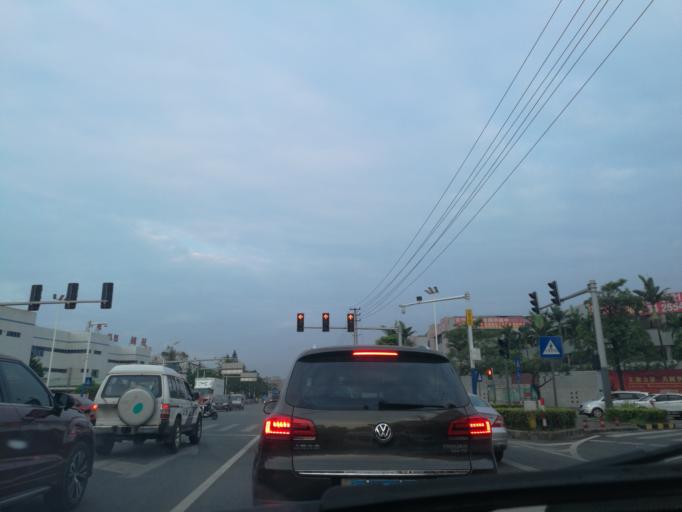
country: CN
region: Guangdong
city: Hengli
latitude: 23.0221
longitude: 113.9854
